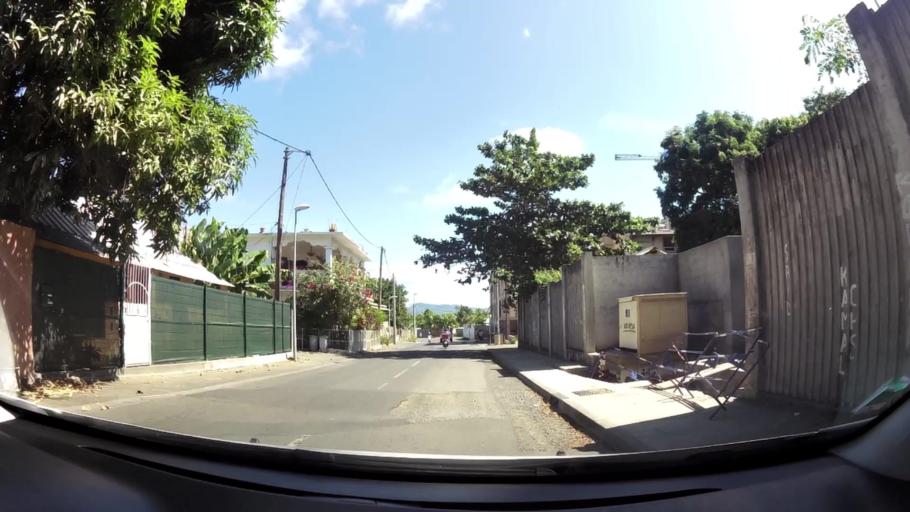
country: YT
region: Pamandzi
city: Pamandzi
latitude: -12.7965
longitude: 45.2797
